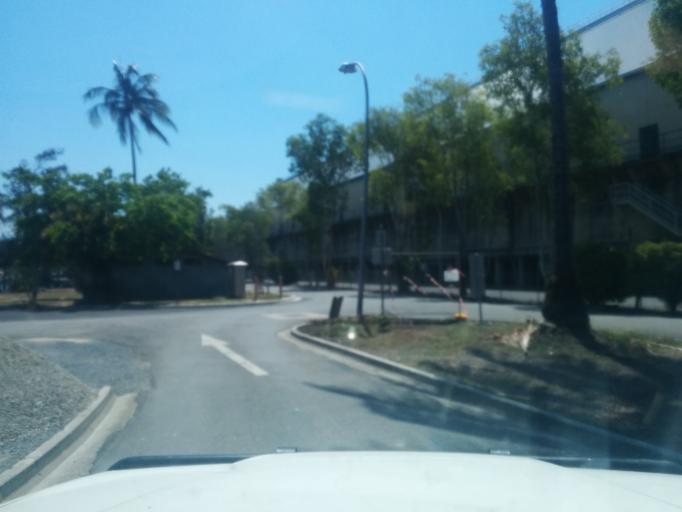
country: AU
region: Queensland
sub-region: Cairns
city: Cairns
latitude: -16.9399
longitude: 145.7775
